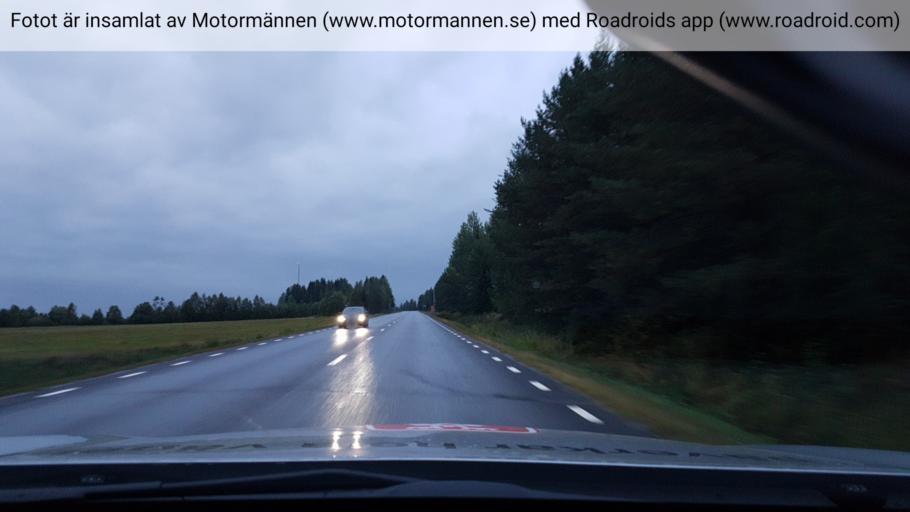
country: SE
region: Vaesterbotten
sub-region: Umea Kommun
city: Ersmark
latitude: 63.8899
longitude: 20.3102
